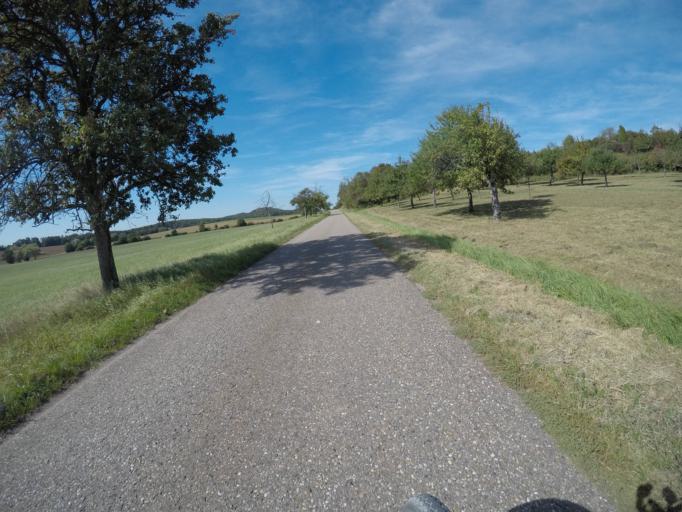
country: DE
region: Baden-Wuerttemberg
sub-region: Karlsruhe Region
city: Sternenfels
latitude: 49.0194
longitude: 8.8698
